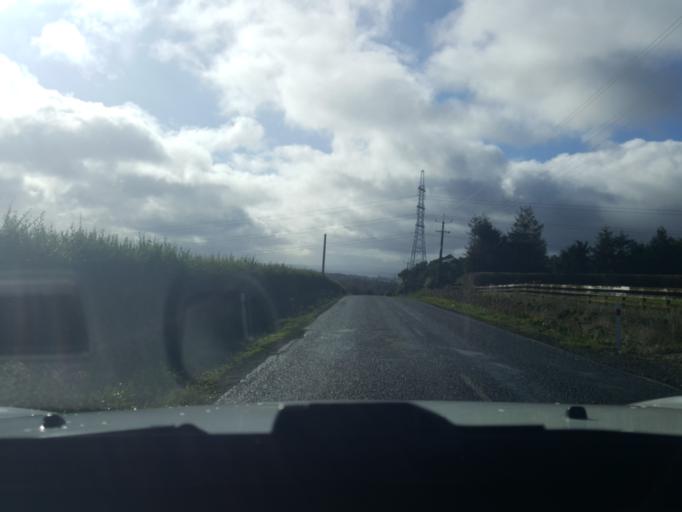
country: NZ
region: Auckland
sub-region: Auckland
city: Pukekohe East
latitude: -37.3085
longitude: 174.9939
